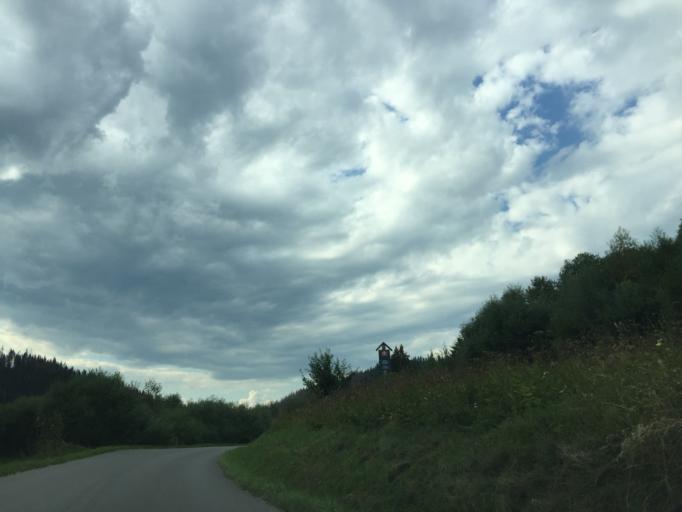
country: SK
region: Zilinsky
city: Namestovo
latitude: 49.3849
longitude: 19.3565
